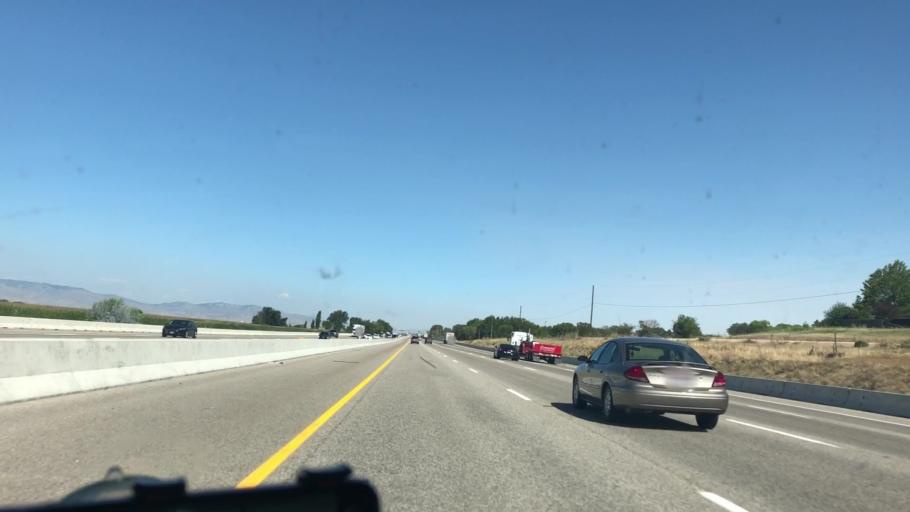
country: US
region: Idaho
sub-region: Ada County
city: Meridian
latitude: 43.5983
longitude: -116.4844
